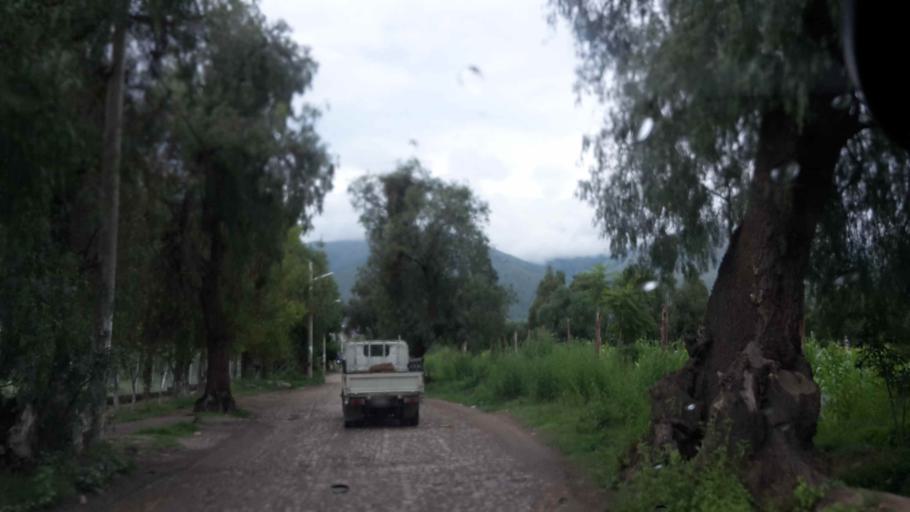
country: BO
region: Cochabamba
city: Cochabamba
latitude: -17.3646
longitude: -66.2134
